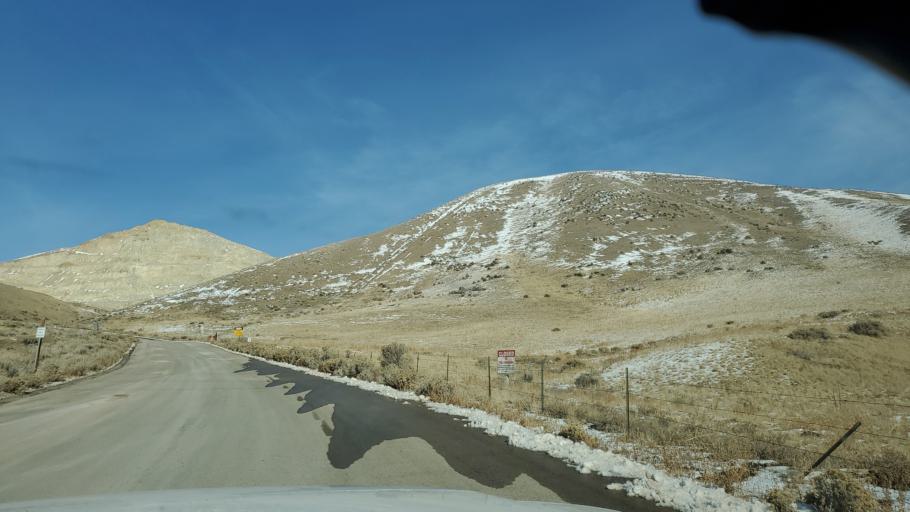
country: US
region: Utah
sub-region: Salt Lake County
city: Bluffdale
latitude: 40.4567
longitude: -111.8954
